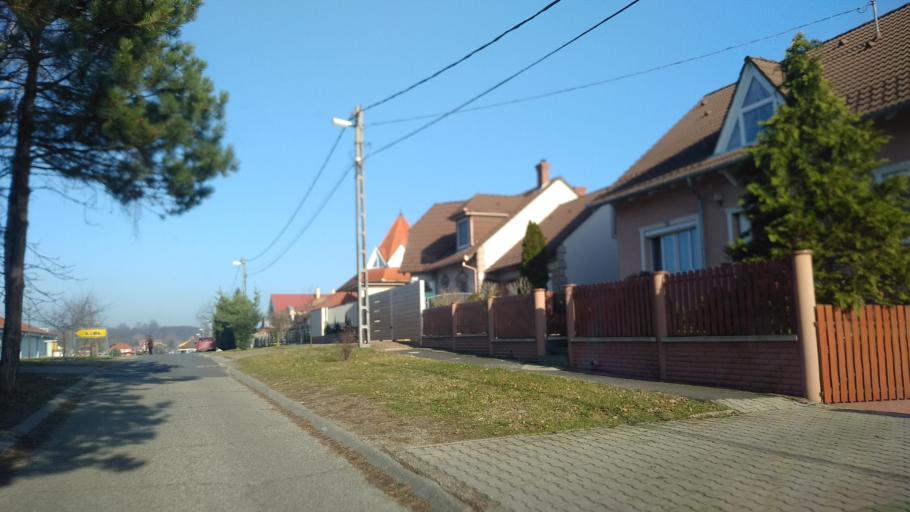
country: HU
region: Somogy
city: Barcs
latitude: 45.9615
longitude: 17.4681
